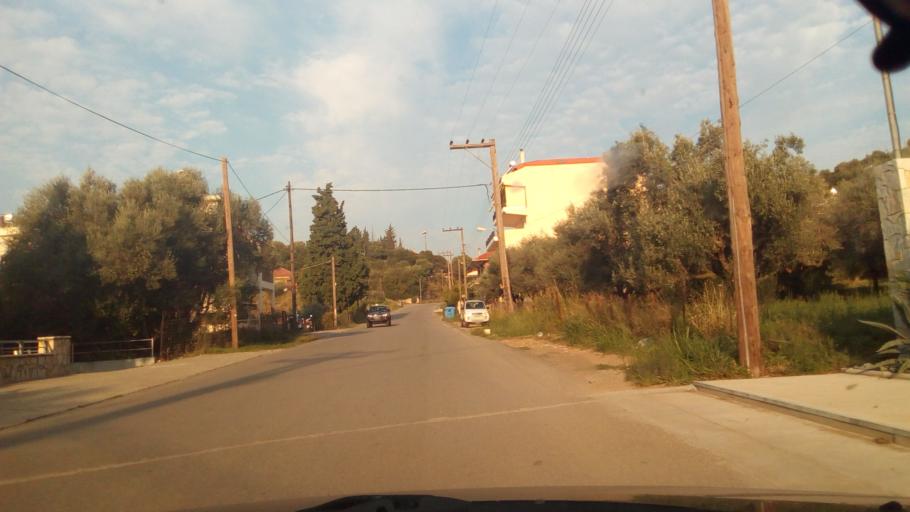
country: GR
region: West Greece
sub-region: Nomos Aitolias kai Akarnanias
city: Nafpaktos
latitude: 38.3936
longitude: 21.8147
